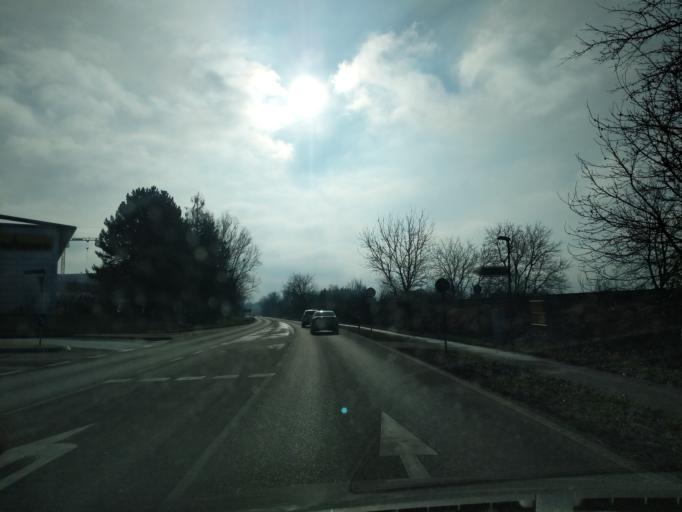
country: DE
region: Baden-Wuerttemberg
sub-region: Tuebingen Region
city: Markdorf
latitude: 47.7081
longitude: 9.3994
